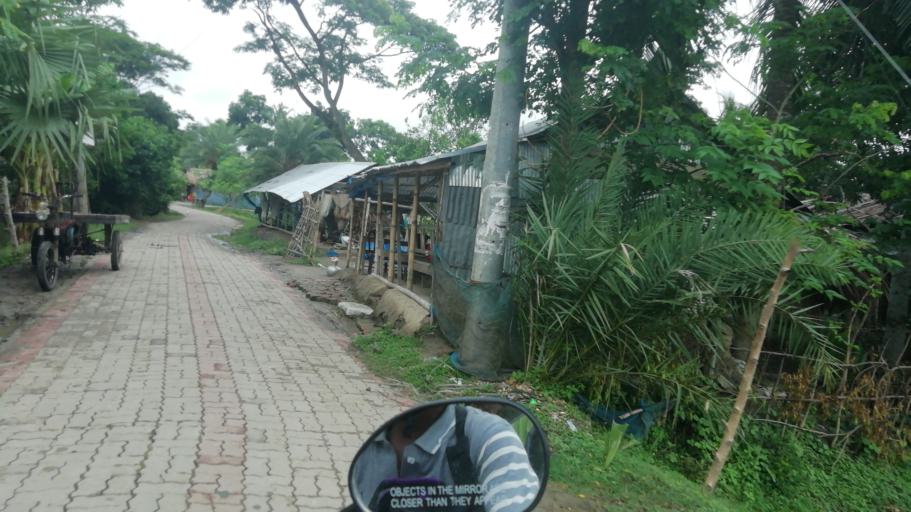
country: BD
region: Khulna
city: Phultala
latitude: 22.5172
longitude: 89.5649
